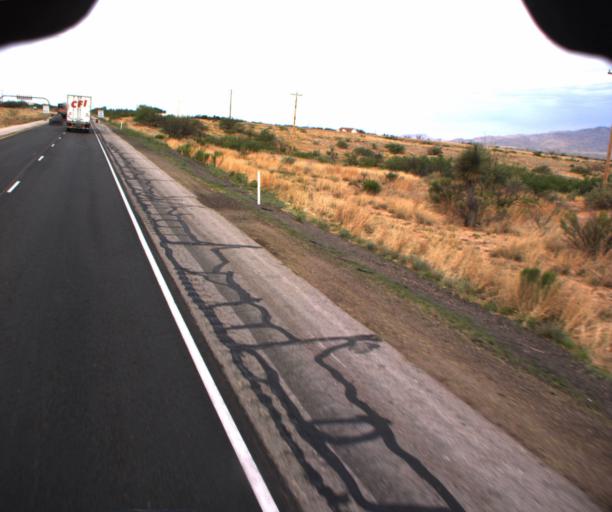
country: US
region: Arizona
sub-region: Cochise County
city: Whetstone
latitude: 31.9634
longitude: -110.3721
